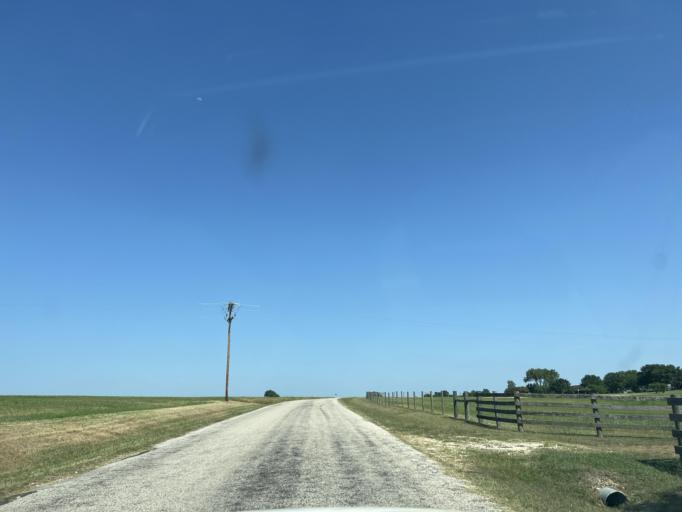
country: US
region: Texas
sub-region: Washington County
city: Brenham
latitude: 30.1687
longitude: -96.3322
